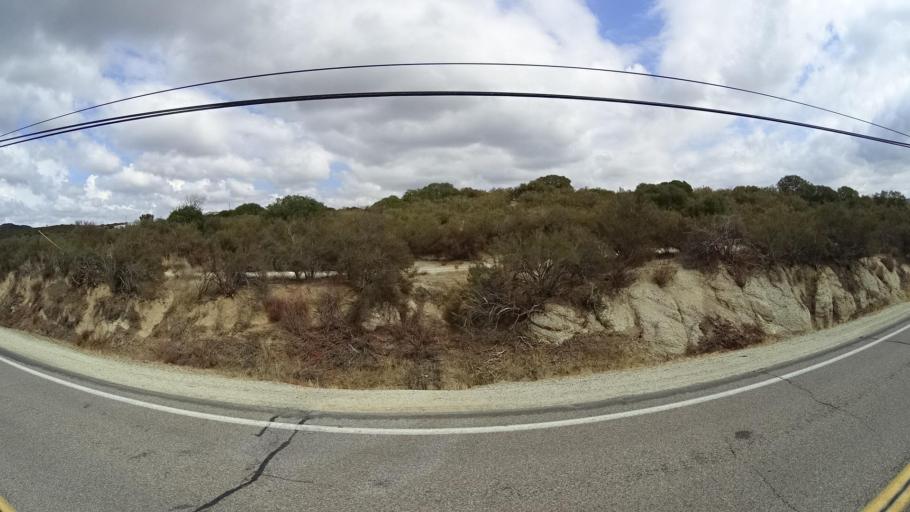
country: US
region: California
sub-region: San Diego County
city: Campo
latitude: 32.6368
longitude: -116.4787
